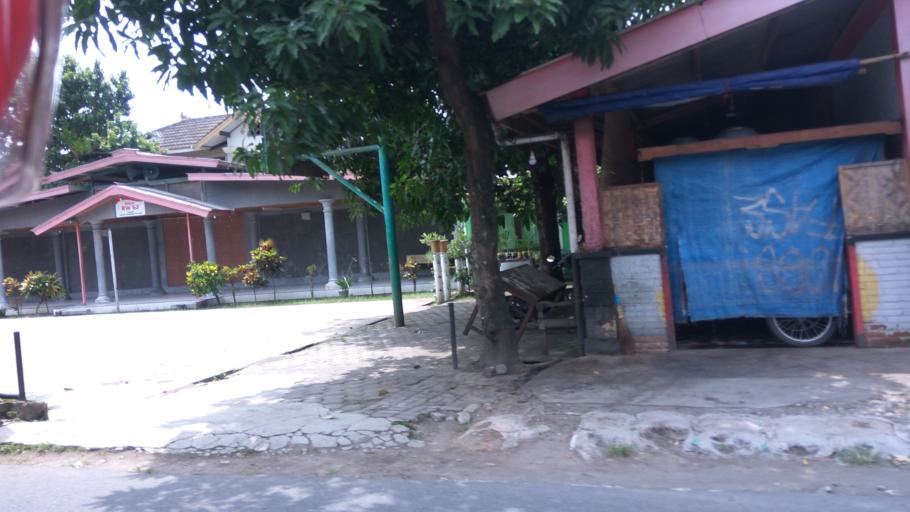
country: ID
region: Daerah Istimewa Yogyakarta
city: Depok
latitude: -7.7453
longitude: 110.4135
